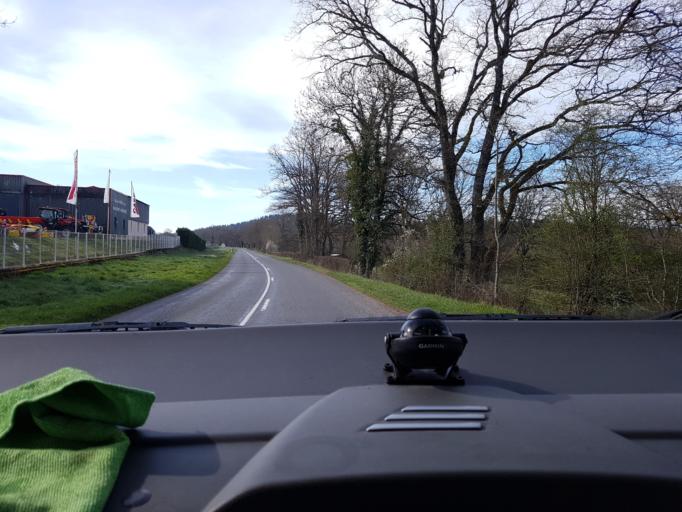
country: FR
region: Bourgogne
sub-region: Departement de Saone-et-Loire
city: Toulon-sur-Arroux
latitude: 46.7300
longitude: 4.1299
